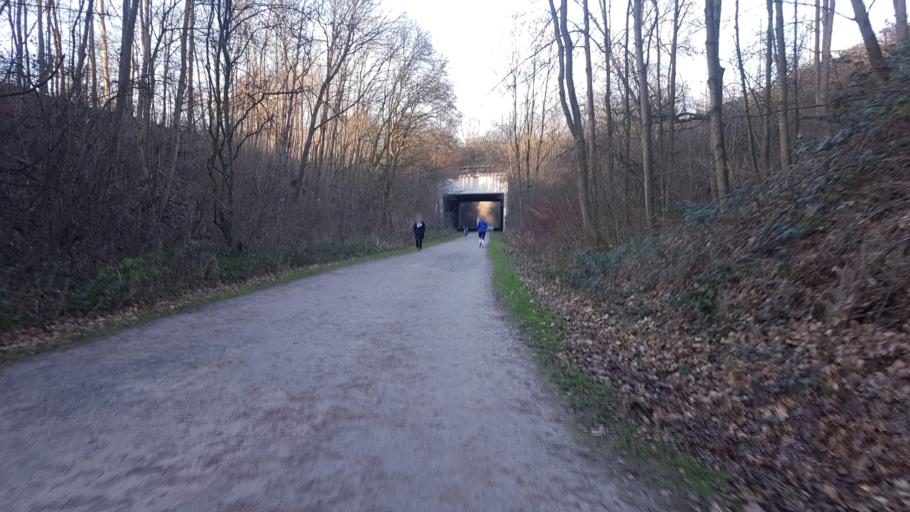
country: DE
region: North Rhine-Westphalia
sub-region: Regierungsbezirk Dusseldorf
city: Essen
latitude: 51.4394
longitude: 6.9591
